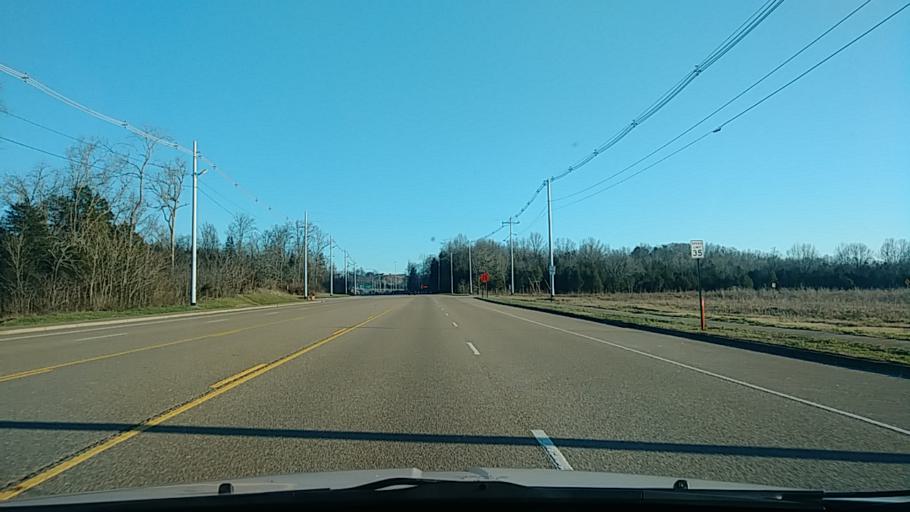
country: US
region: Tennessee
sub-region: Hamblen County
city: Morristown
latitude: 36.1827
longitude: -83.3537
